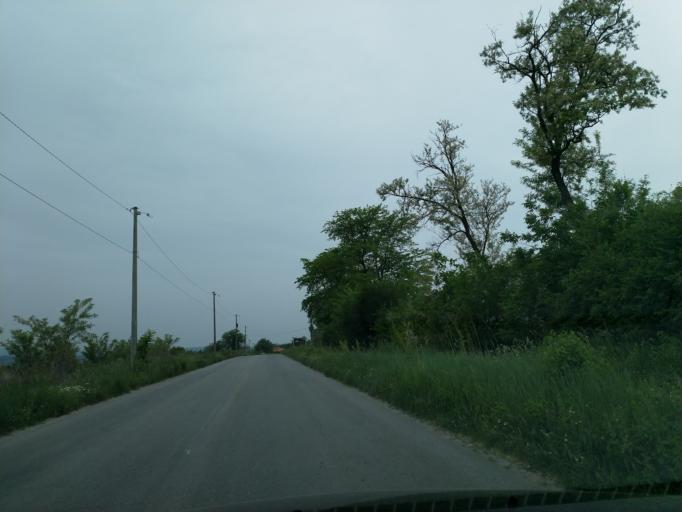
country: RS
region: Central Serbia
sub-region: Pomoravski Okrug
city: Jagodina
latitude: 43.9726
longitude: 21.2373
